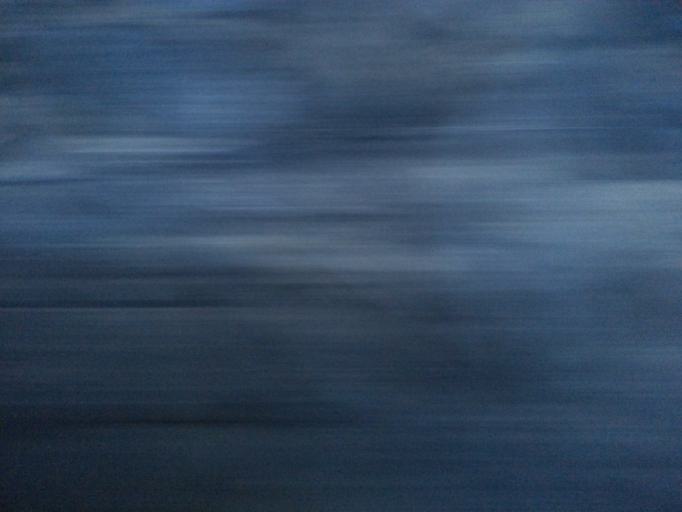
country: NO
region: Sor-Trondelag
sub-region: Rennebu
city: Berkak
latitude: 62.6957
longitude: 9.9434
